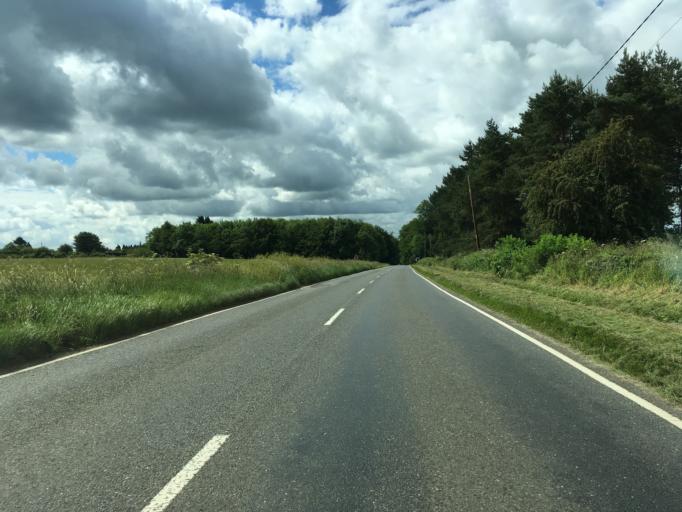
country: GB
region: England
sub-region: Oxfordshire
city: Chipping Norton
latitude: 51.9239
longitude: -1.5414
